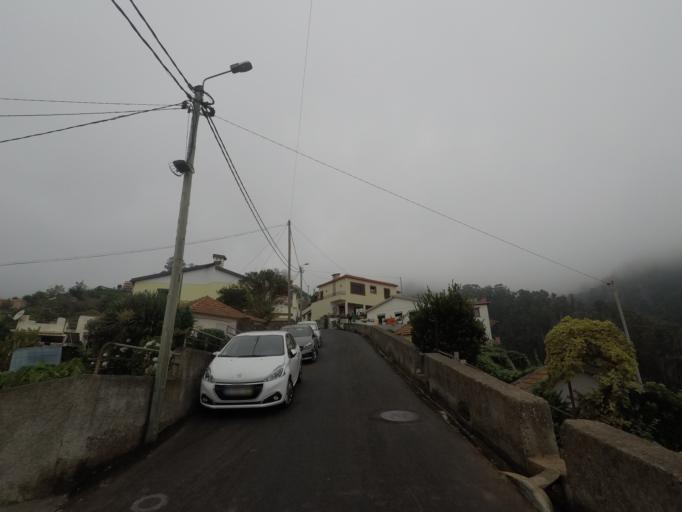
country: PT
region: Madeira
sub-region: Camara de Lobos
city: Curral das Freiras
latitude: 32.6833
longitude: -16.9470
